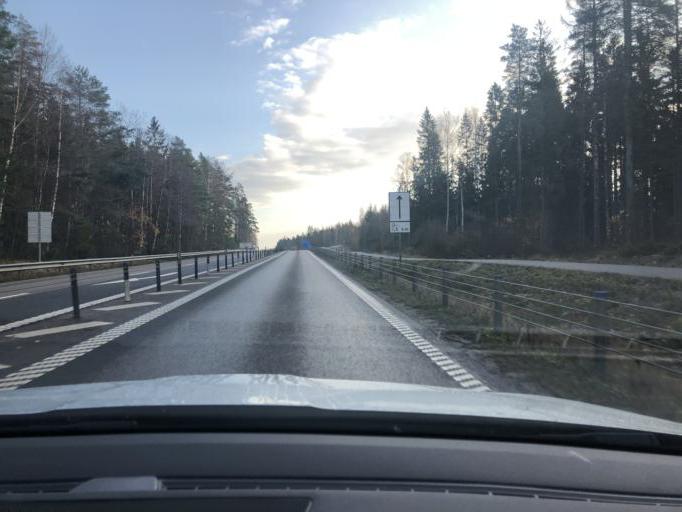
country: SE
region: Soedermanland
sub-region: Katrineholms Kommun
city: Katrineholm
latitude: 59.0112
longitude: 16.2650
